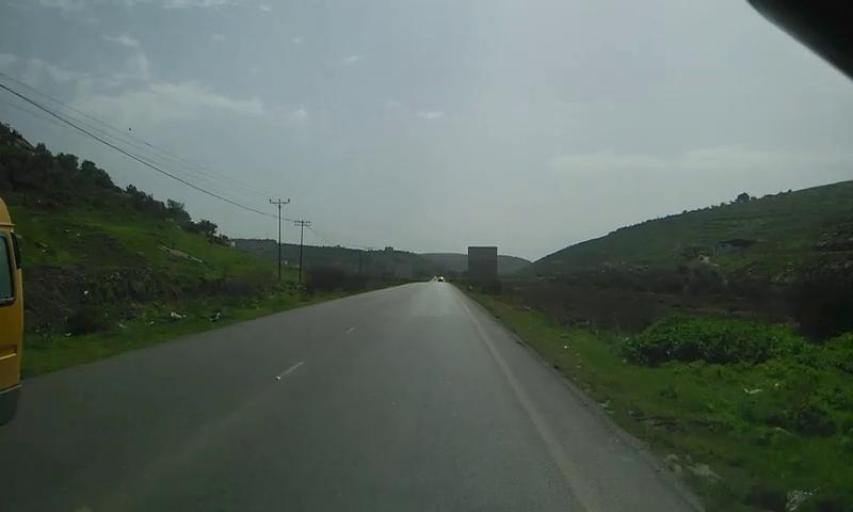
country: PS
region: West Bank
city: Mirkah
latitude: 32.3976
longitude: 35.2228
